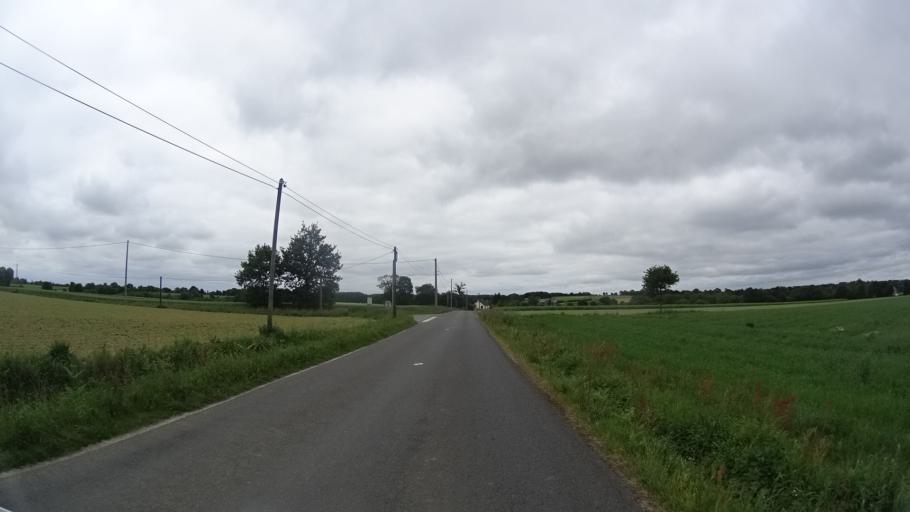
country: FR
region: Brittany
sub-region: Departement d'Ille-et-Vilaine
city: Pleumeleuc
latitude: 48.1950
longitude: -1.9088
